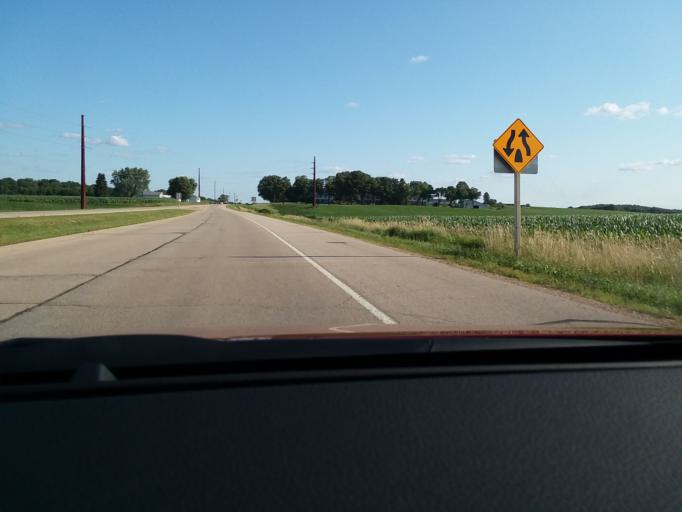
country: US
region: Wisconsin
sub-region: Dane County
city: Waunakee
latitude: 43.1871
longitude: -89.4119
